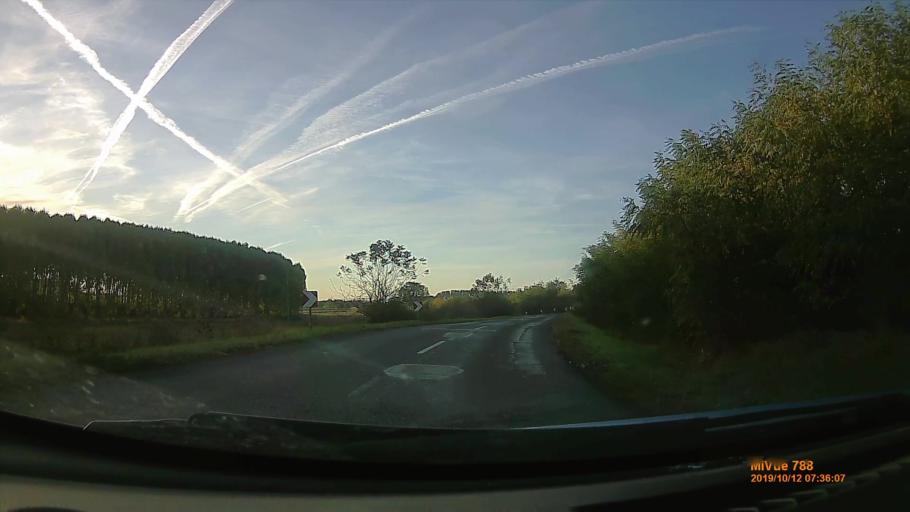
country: HU
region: Hajdu-Bihar
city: Pocsaj
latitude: 47.2481
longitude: 21.8124
